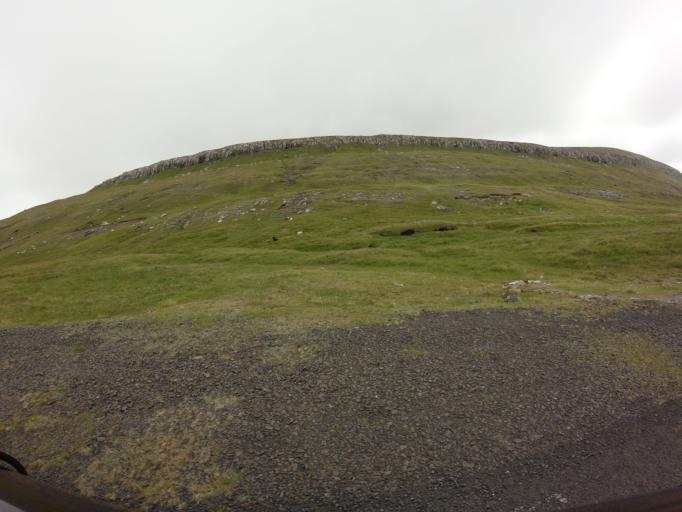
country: FO
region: Sandoy
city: Sandur
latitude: 61.8126
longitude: -6.7519
